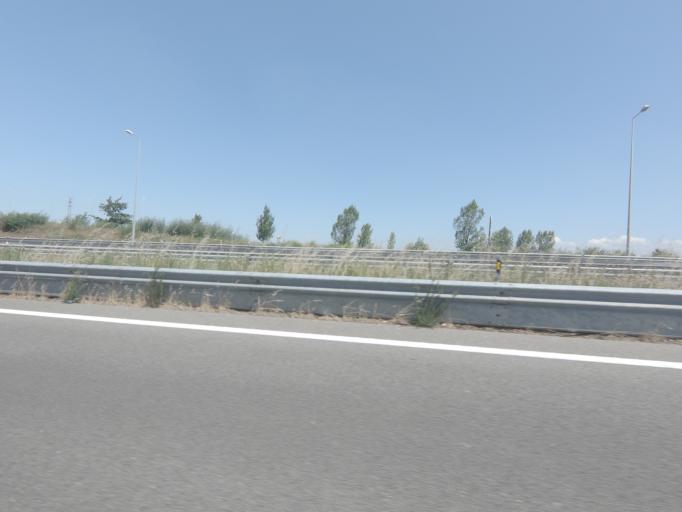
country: PT
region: Porto
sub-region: Matosinhos
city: Sao Mamede de Infesta
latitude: 41.2003
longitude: -8.6074
